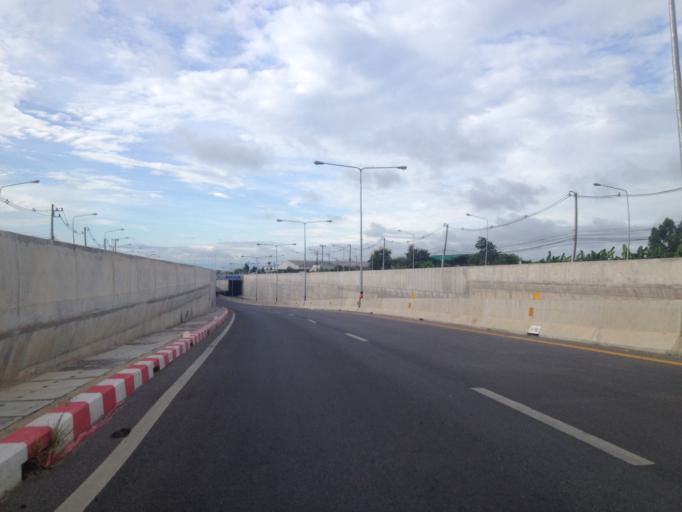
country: TH
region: Chiang Mai
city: Mae Wang
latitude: 18.6084
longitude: 98.8351
